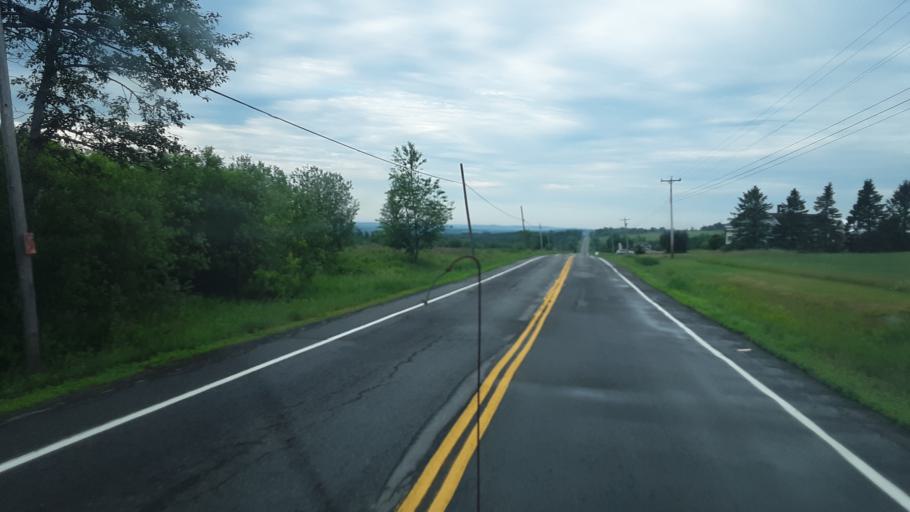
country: US
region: Maine
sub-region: Penobscot County
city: Patten
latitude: 46.0431
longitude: -68.4438
